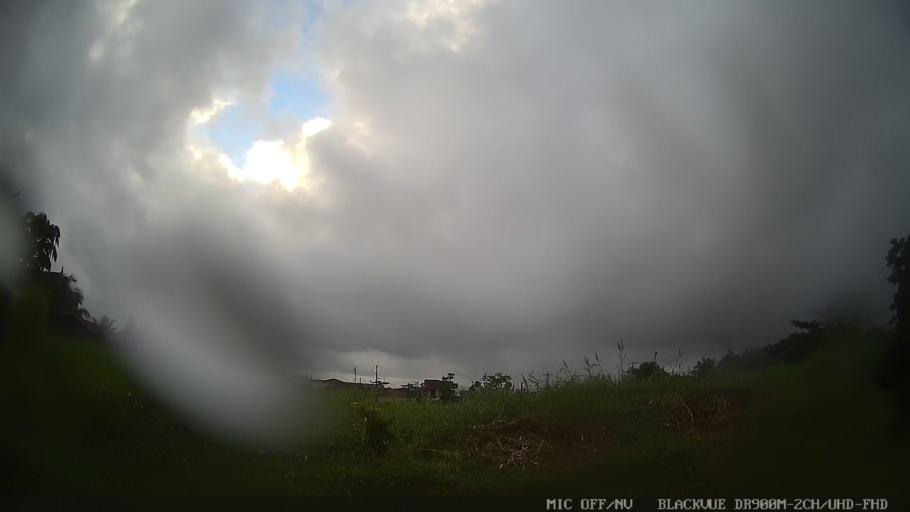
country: BR
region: Sao Paulo
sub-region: Itanhaem
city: Itanhaem
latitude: -24.2060
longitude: -46.8392
